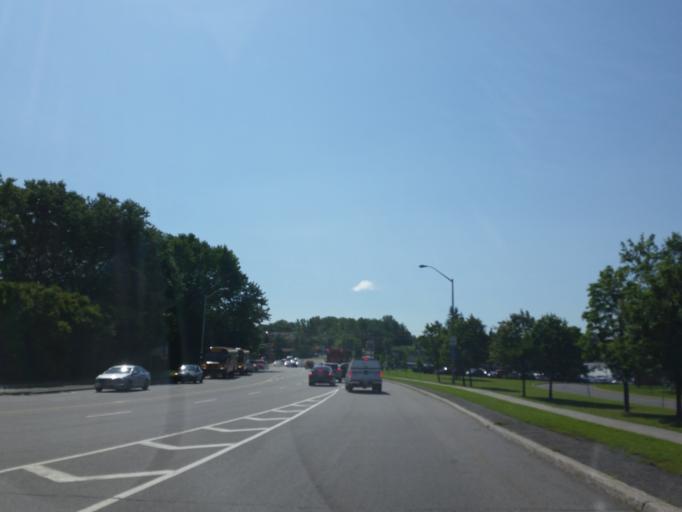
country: CA
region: Quebec
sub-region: Outaouais
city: Gatineau
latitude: 45.4674
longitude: -75.5448
